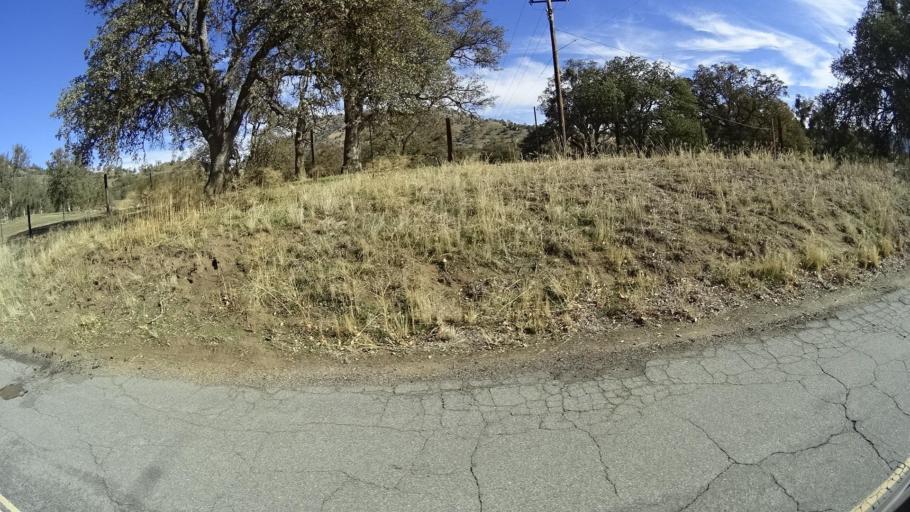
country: US
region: California
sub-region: Kern County
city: Alta Sierra
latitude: 35.6287
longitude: -118.7498
